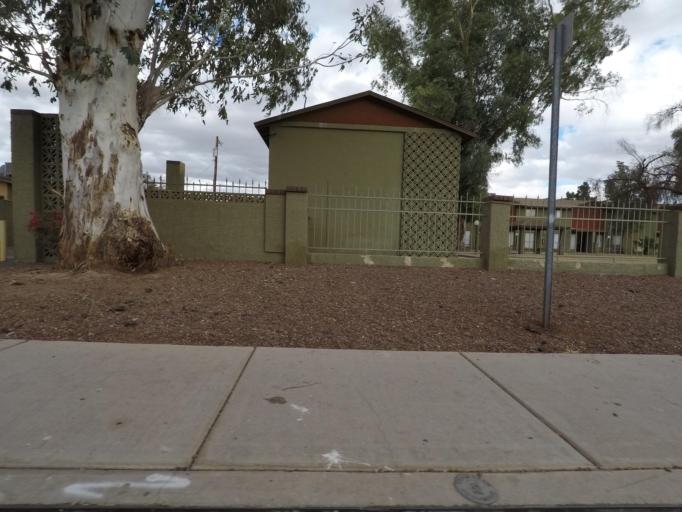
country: US
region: Arizona
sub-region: Maricopa County
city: Glendale
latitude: 33.5045
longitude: -112.1429
